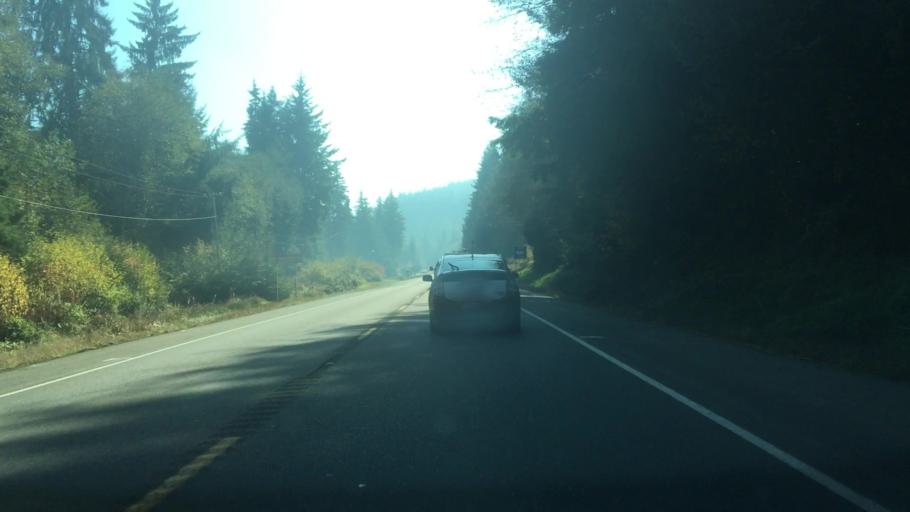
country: US
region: Washington
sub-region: Grays Harbor County
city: Central Park
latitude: 46.9232
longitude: -123.7174
